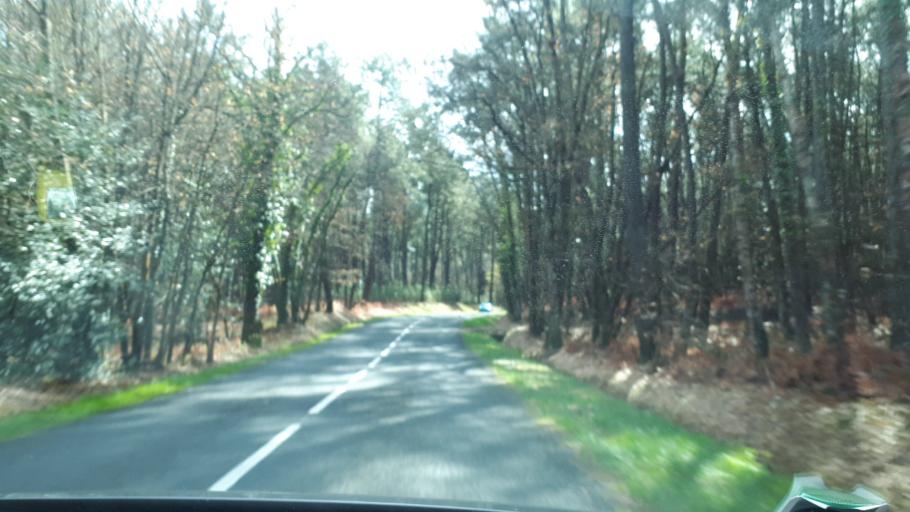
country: FR
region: Pays de la Loire
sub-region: Departement de la Sarthe
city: Brette-les-Pins
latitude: 47.8656
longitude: 0.3587
